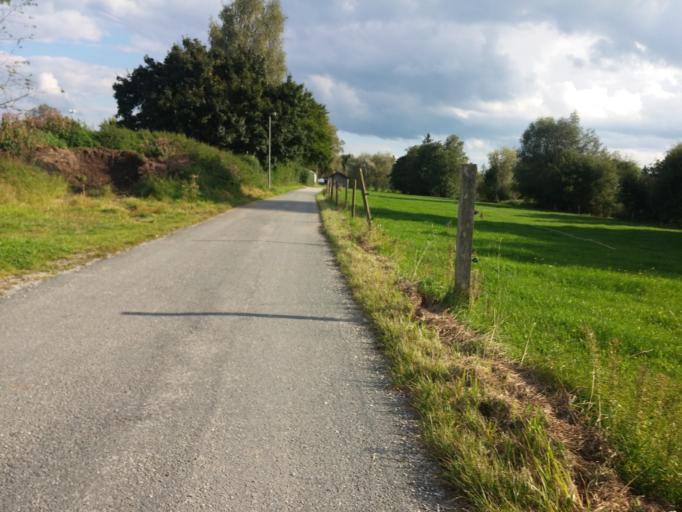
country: DE
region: Bavaria
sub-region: Upper Bavaria
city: Grafing bei Munchen
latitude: 48.0519
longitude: 11.9670
